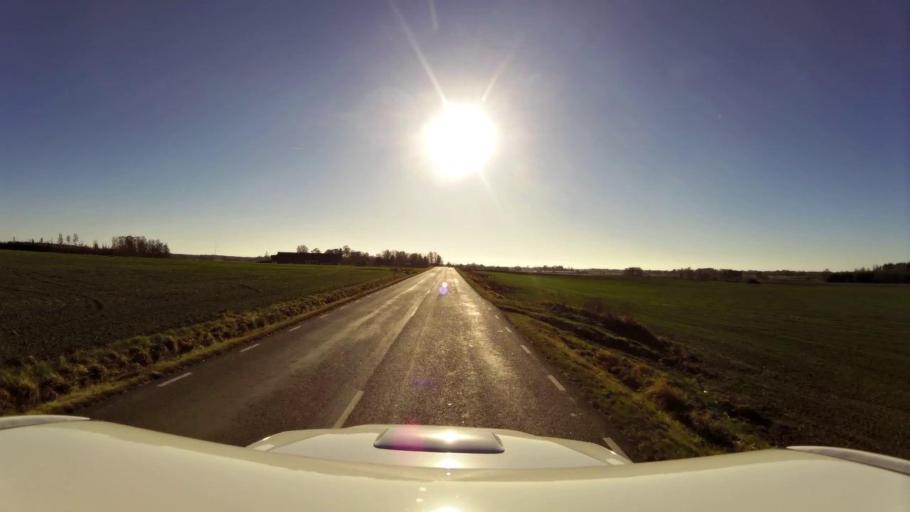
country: SE
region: OEstergoetland
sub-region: Linkopings Kommun
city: Malmslatt
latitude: 58.3553
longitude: 15.5631
